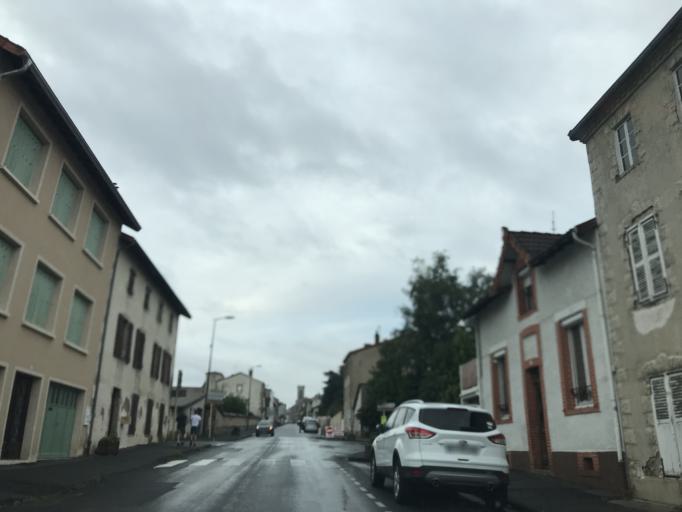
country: FR
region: Auvergne
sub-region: Departement du Puy-de-Dome
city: Arlanc
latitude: 45.4180
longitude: 3.7246
